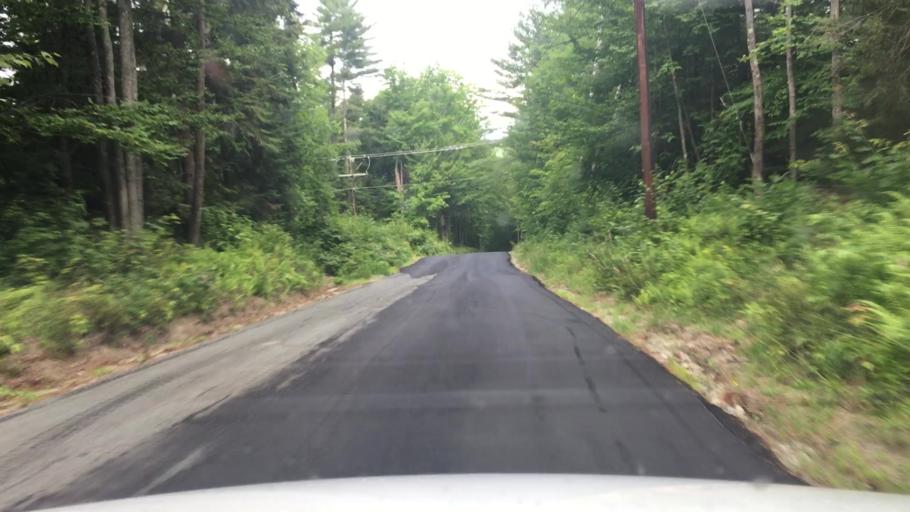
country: US
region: New Hampshire
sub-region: Grafton County
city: Deerfield
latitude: 44.2869
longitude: -71.6593
